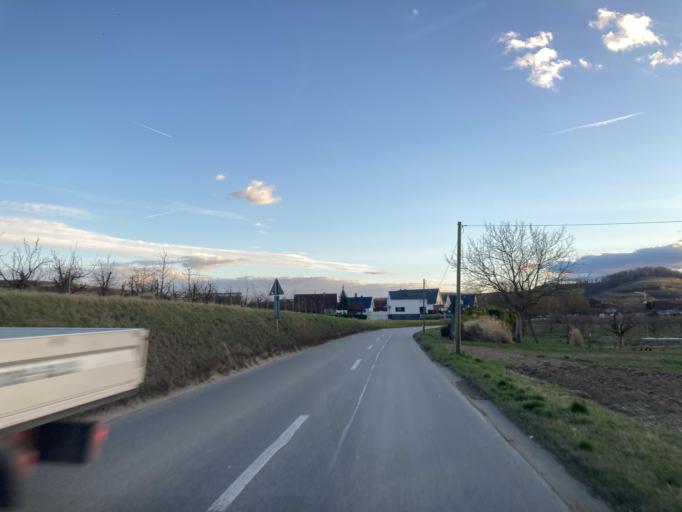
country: DE
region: Baden-Wuerttemberg
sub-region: Freiburg Region
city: Sasbach
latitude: 48.1249
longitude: 7.6083
